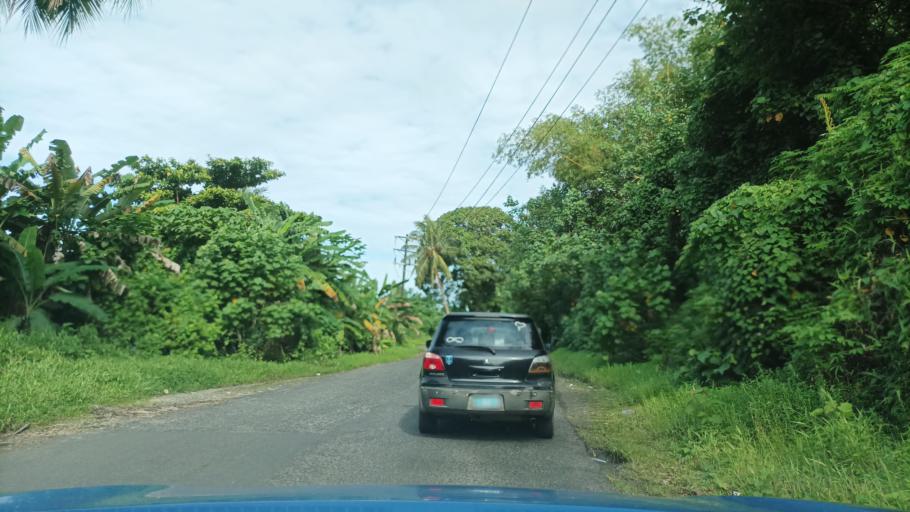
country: FM
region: Pohnpei
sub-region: Kolonia Municipality
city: Kolonia
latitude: 6.9540
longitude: 158.2280
